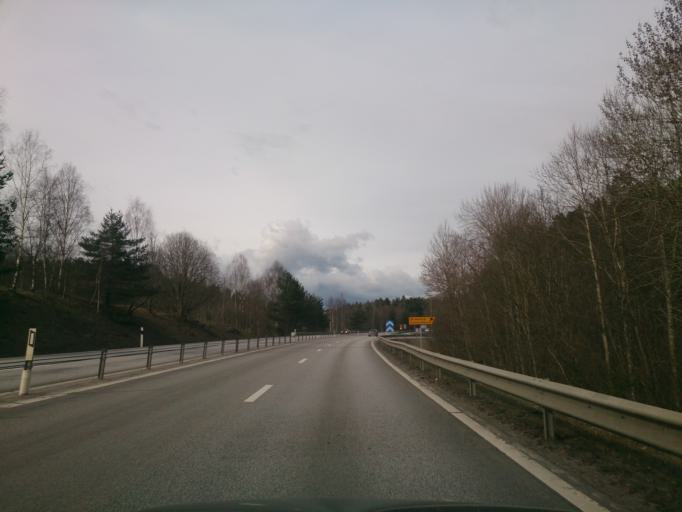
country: SE
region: OEstergoetland
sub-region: Norrkopings Kommun
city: Jursla
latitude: 58.6845
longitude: 16.1499
